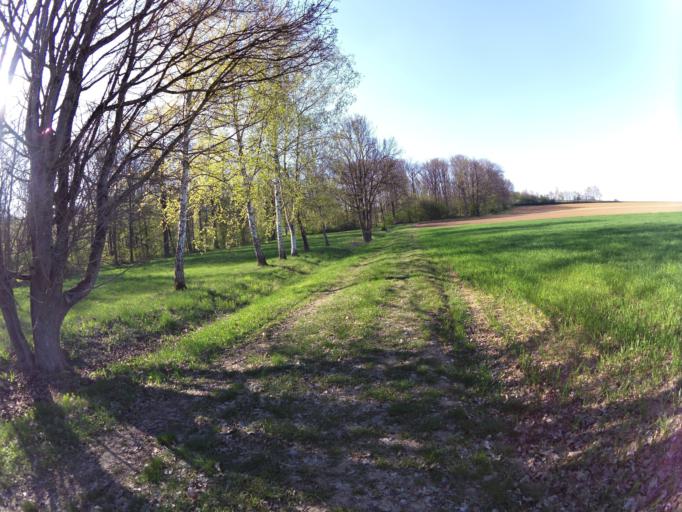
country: DE
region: Bavaria
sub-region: Regierungsbezirk Unterfranken
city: Rimpar
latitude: 49.8717
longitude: 9.9935
